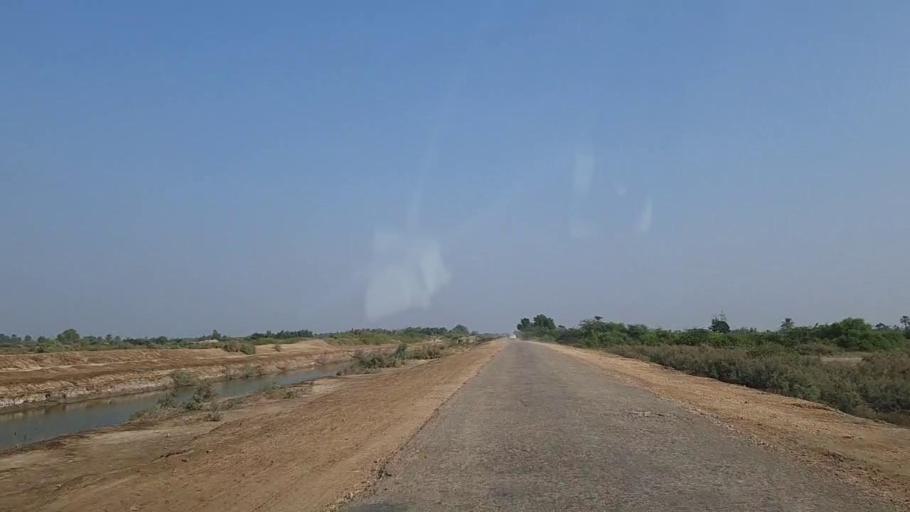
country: PK
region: Sindh
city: Mirpur Sakro
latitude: 24.6339
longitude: 67.6155
